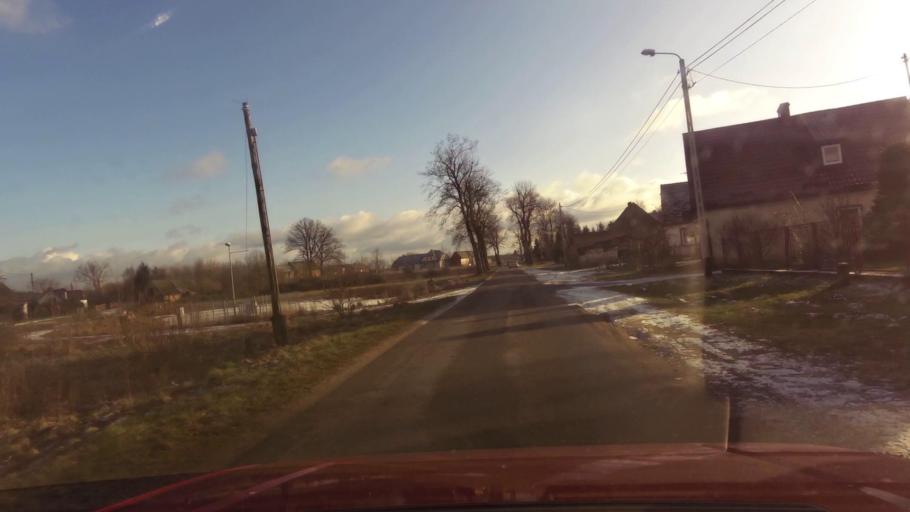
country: PL
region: West Pomeranian Voivodeship
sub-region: Powiat bialogardzki
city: Bialogard
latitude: 54.0809
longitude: 16.0880
